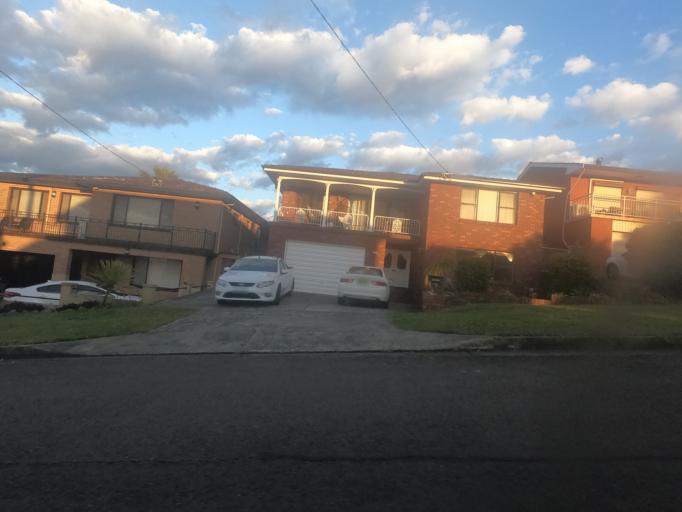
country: AU
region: New South Wales
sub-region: Wollongong
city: Koonawarra
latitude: -34.4947
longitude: 150.8131
